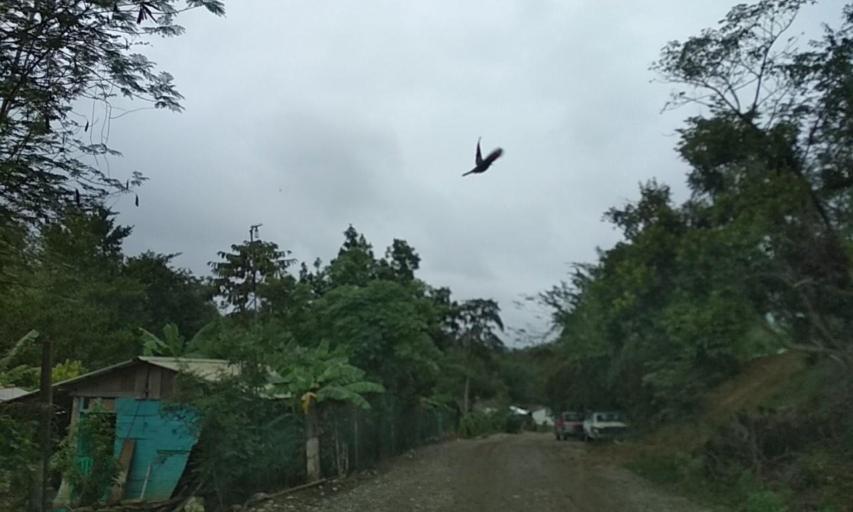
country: MX
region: Veracruz
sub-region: Papantla
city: El Chote
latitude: 20.3817
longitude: -97.3520
